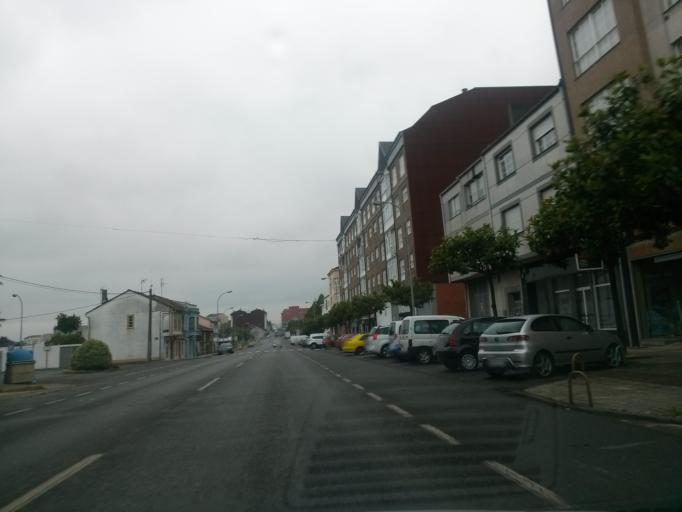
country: ES
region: Galicia
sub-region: Provincia de Lugo
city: Rabade
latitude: 43.1227
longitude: -7.6325
